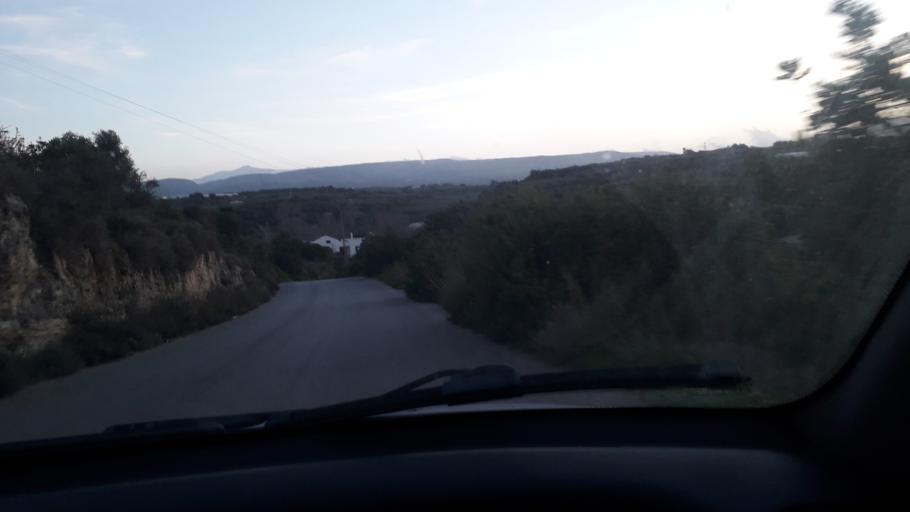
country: GR
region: Crete
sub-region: Nomos Rethymnis
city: Panormos
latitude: 35.3826
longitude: 24.6236
